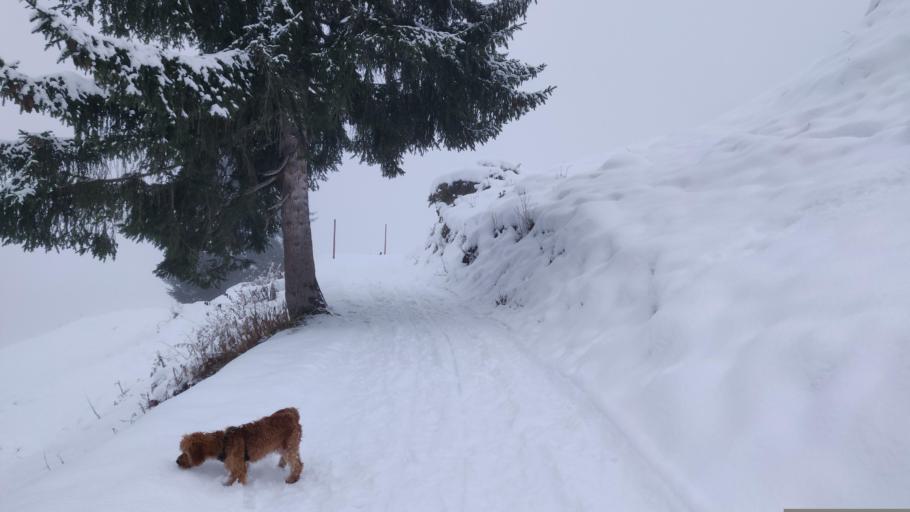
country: CH
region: Bern
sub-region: Interlaken-Oberhasli District
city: Lauterbrunnen
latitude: 46.5920
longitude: 7.8921
